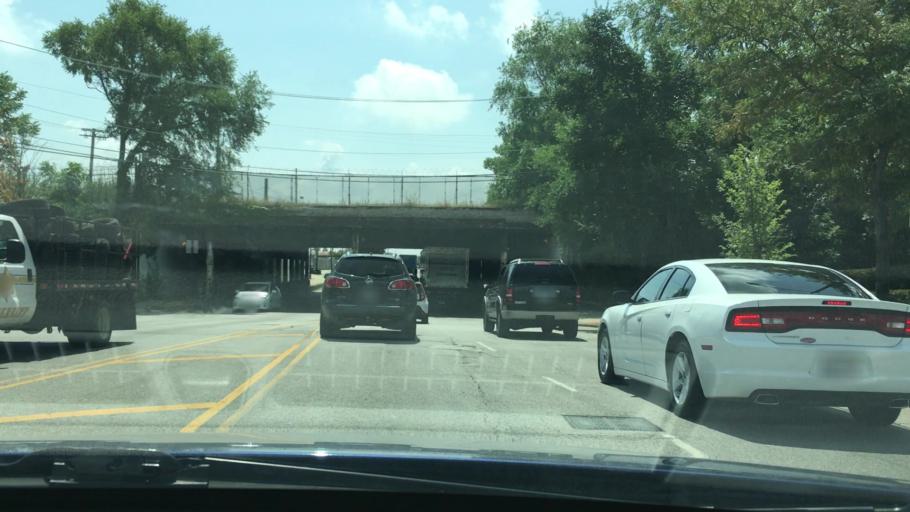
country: US
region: Illinois
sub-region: Cook County
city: Chicago
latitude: 41.8641
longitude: -87.6860
